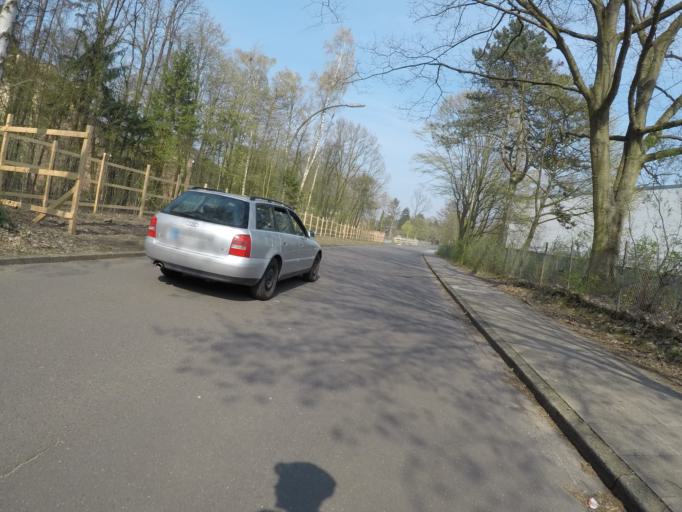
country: DE
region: Hamburg
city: Poppenbuettel
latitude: 53.6599
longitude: 10.0989
